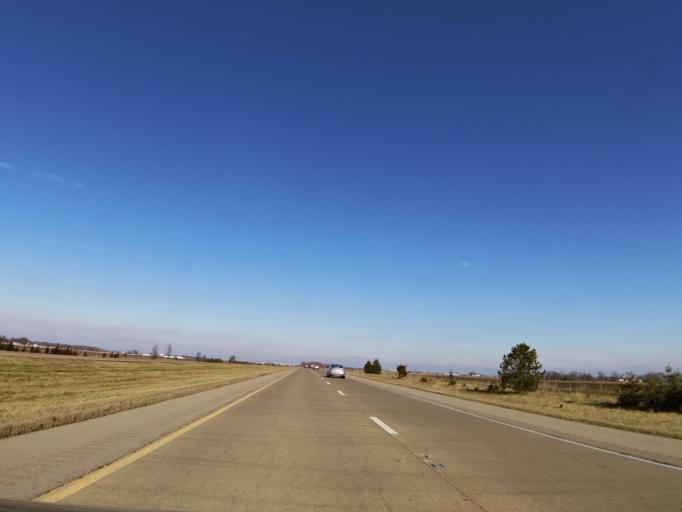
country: US
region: Illinois
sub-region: LaSalle County
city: La Salle
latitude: 41.4303
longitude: -89.0585
